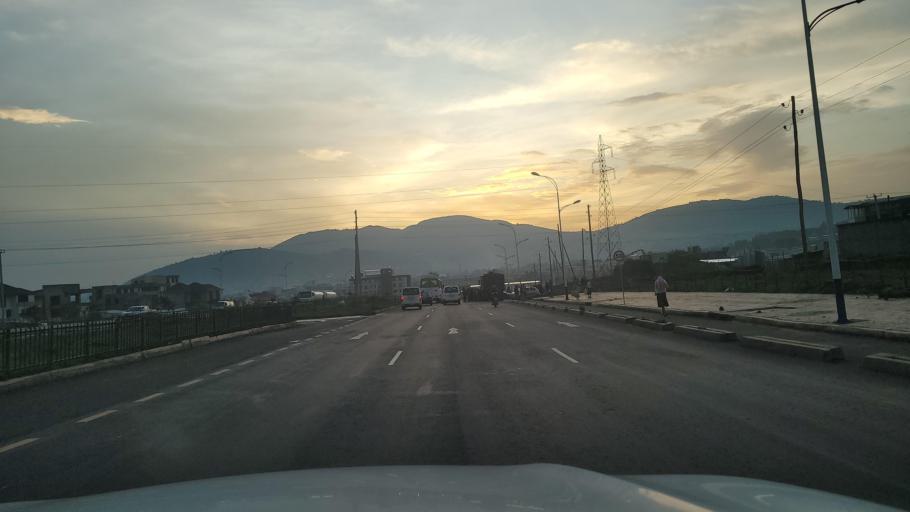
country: ET
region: Adis Abeba
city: Addis Ababa
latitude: 8.9507
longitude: 38.7034
